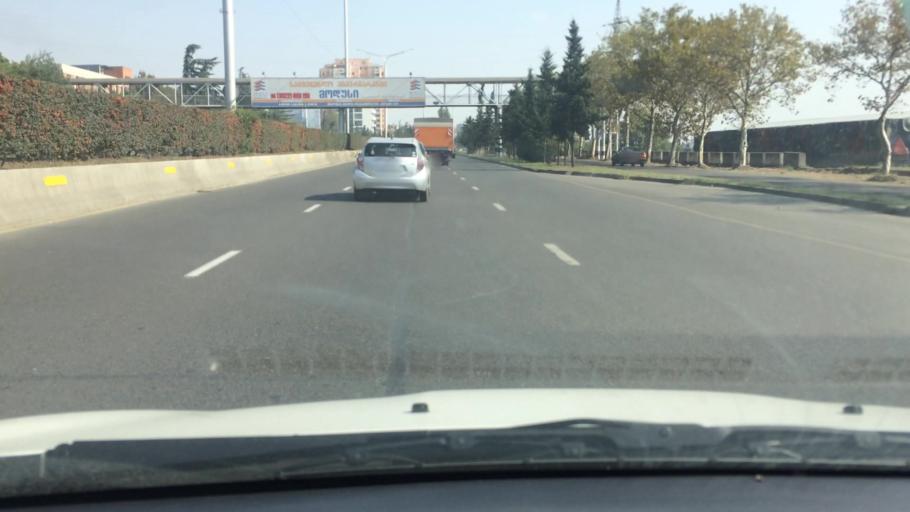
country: GE
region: T'bilisi
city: Tbilisi
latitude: 41.6880
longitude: 44.8480
